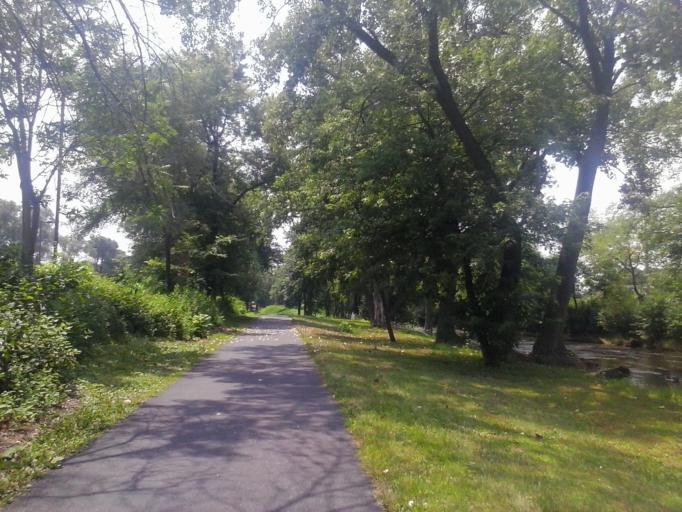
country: US
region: Illinois
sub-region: Will County
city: Lockport
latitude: 41.5845
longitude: -88.0612
